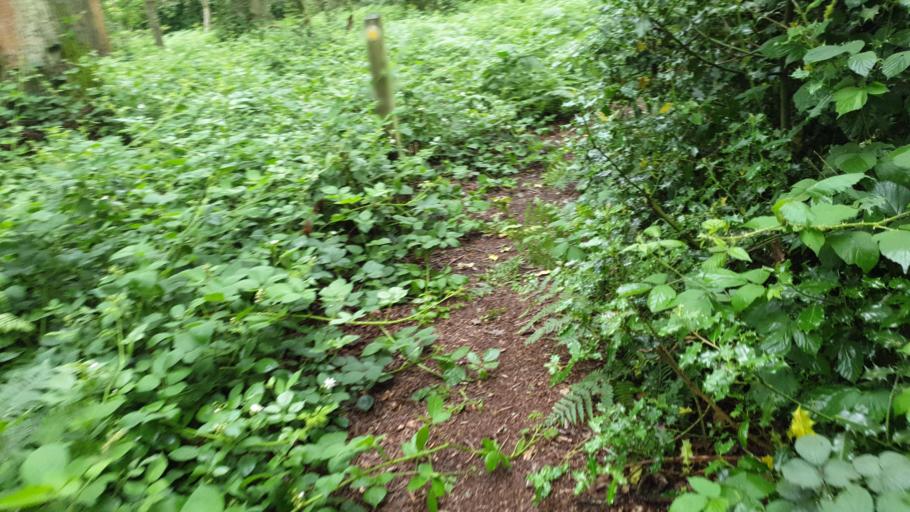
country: GB
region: England
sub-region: Essex
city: Great Bentley
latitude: 51.8849
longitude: 1.1062
